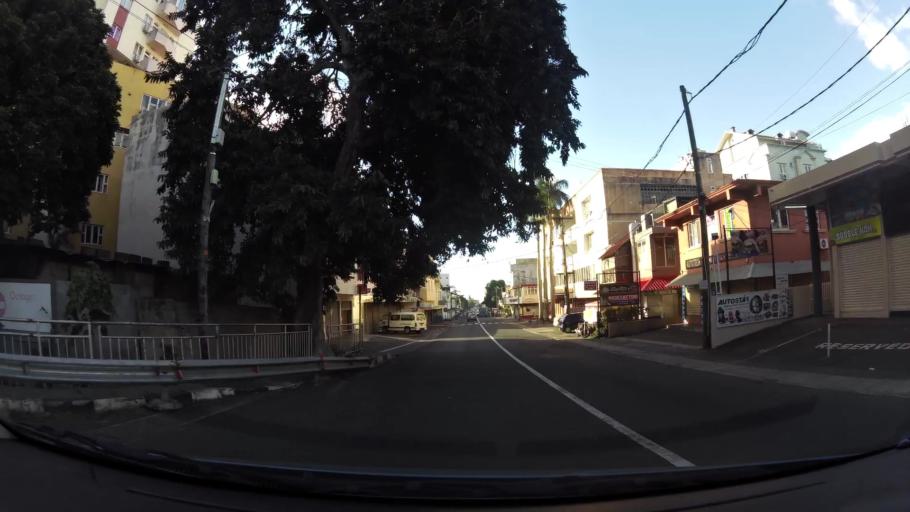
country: MU
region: Plaines Wilhems
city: Ebene
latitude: -20.2302
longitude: 57.4676
